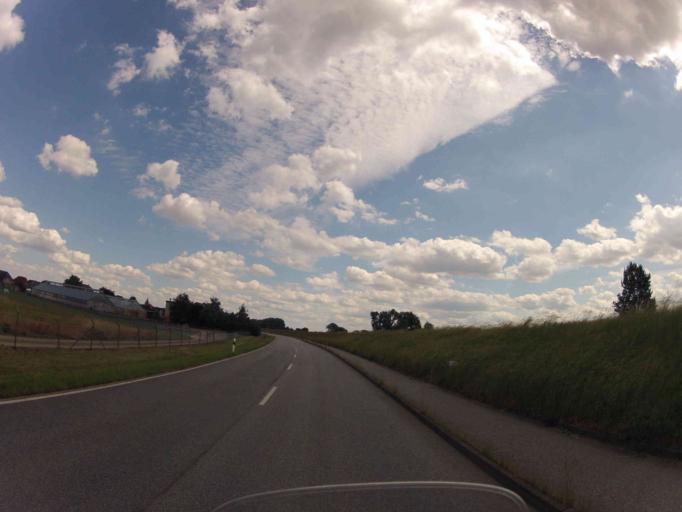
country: DE
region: Lower Saxony
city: Stelle
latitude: 53.4272
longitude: 10.1166
